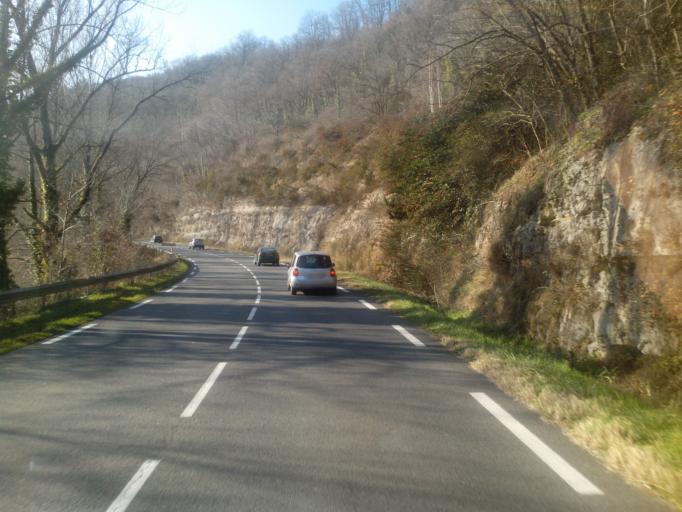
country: FR
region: Midi-Pyrenees
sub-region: Departement de l'Aveyron
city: Capdenac-Gare
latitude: 44.5879
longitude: 2.0836
